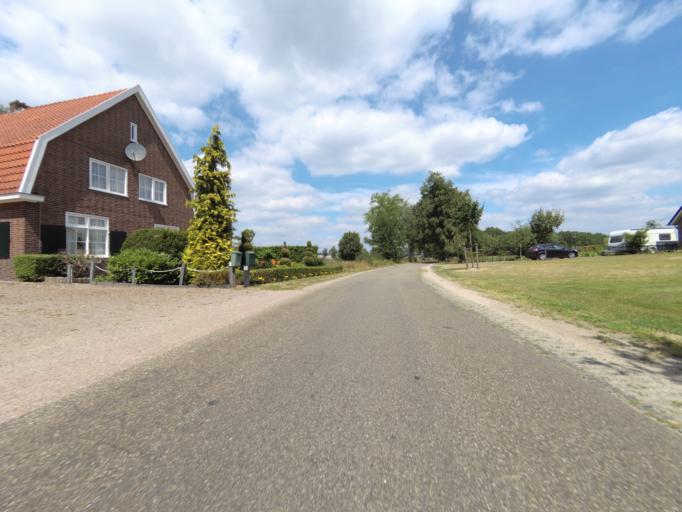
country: NL
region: Overijssel
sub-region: Gemeente Raalte
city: Raalte
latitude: 52.3124
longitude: 6.3003
